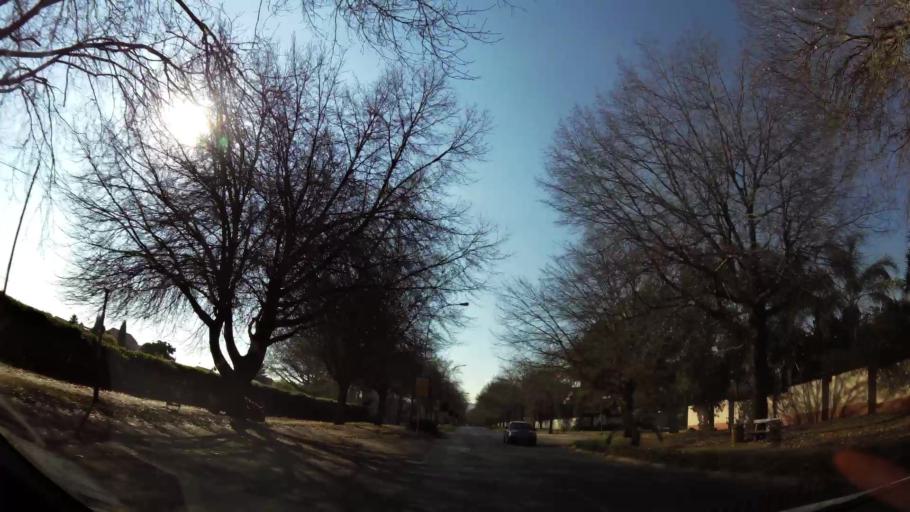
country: ZA
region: Gauteng
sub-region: Ekurhuleni Metropolitan Municipality
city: Germiston
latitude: -26.1706
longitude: 28.1477
